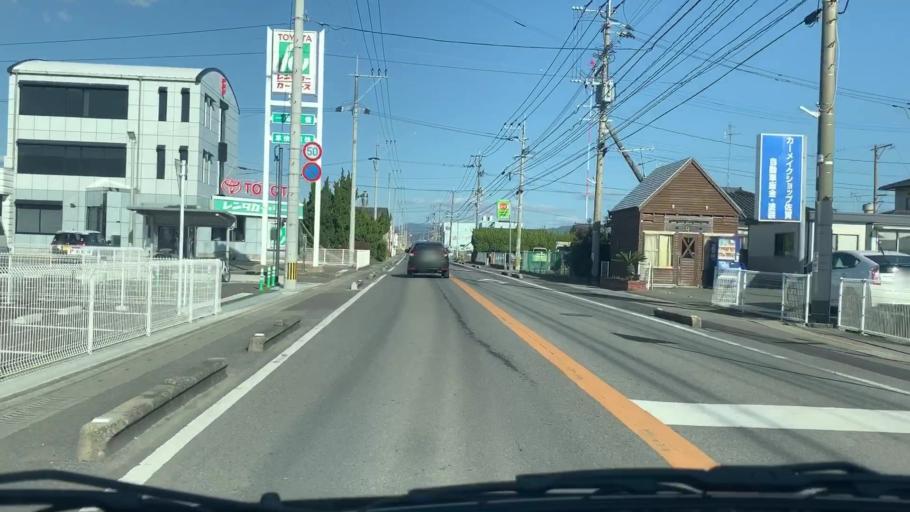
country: JP
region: Saga Prefecture
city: Saga-shi
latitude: 33.2480
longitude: 130.2655
